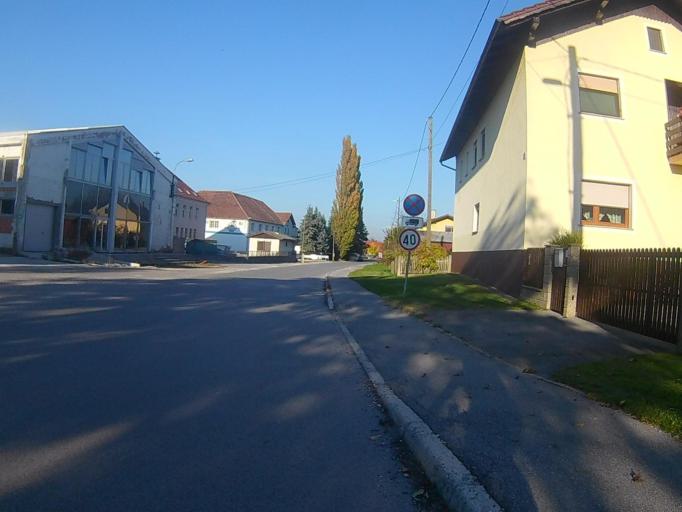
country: SI
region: Hoce-Slivnica
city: Spodnje Hoce
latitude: 46.4990
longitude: 15.6406
